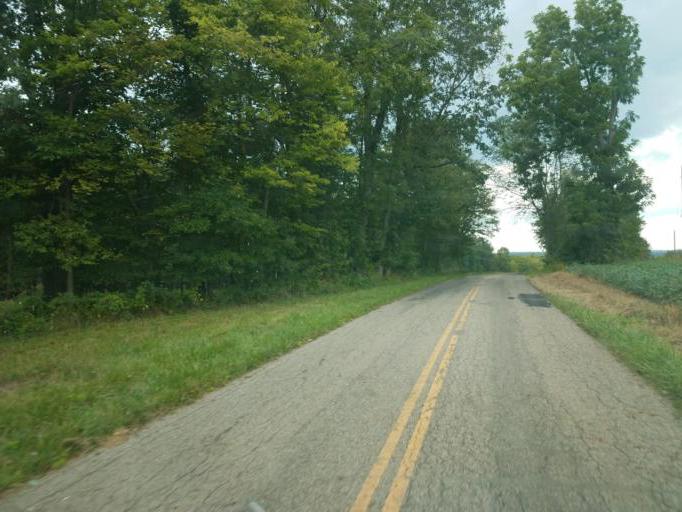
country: US
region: Ohio
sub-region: Knox County
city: Gambier
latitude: 40.3711
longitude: -82.3350
